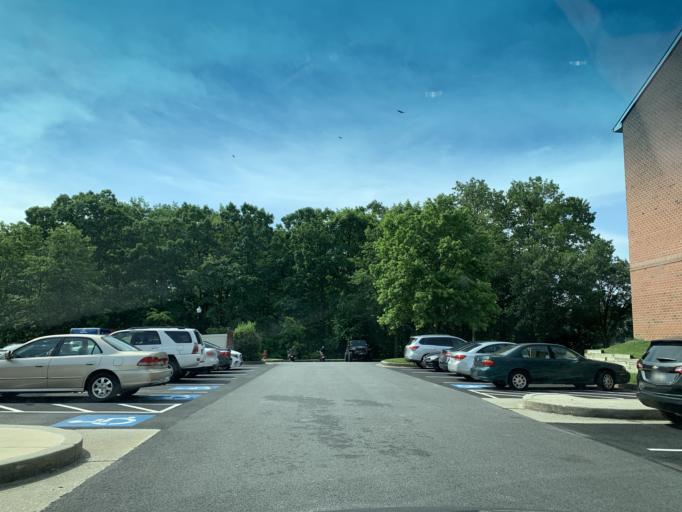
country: US
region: Maryland
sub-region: Baltimore County
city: Perry Hall
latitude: 39.3950
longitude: -76.4774
